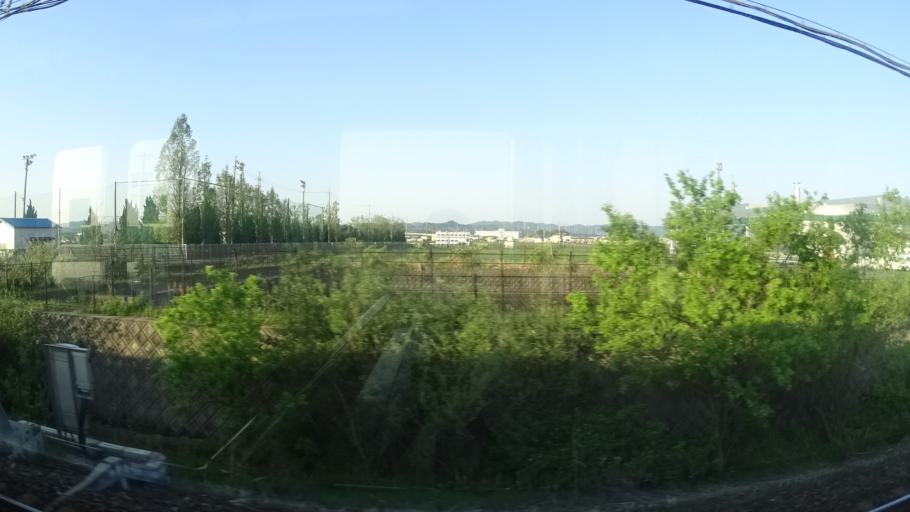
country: JP
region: Mie
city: Hisai-motomachi
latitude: 34.5604
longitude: 136.5564
